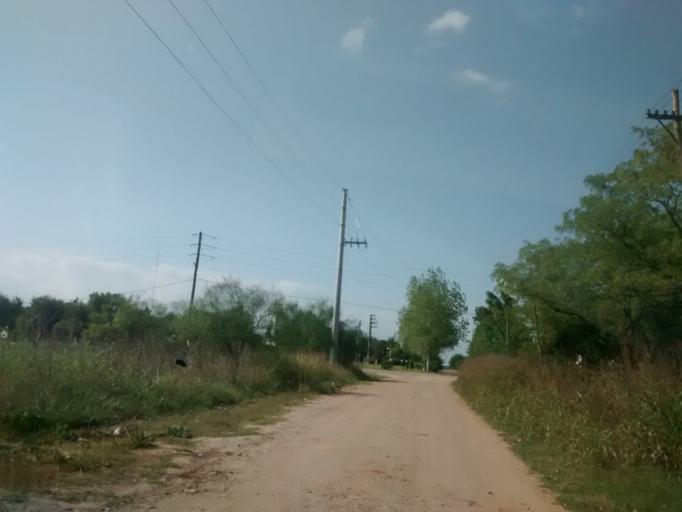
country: AR
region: Buenos Aires
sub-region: Partido de La Plata
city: La Plata
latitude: -35.0039
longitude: -57.9004
